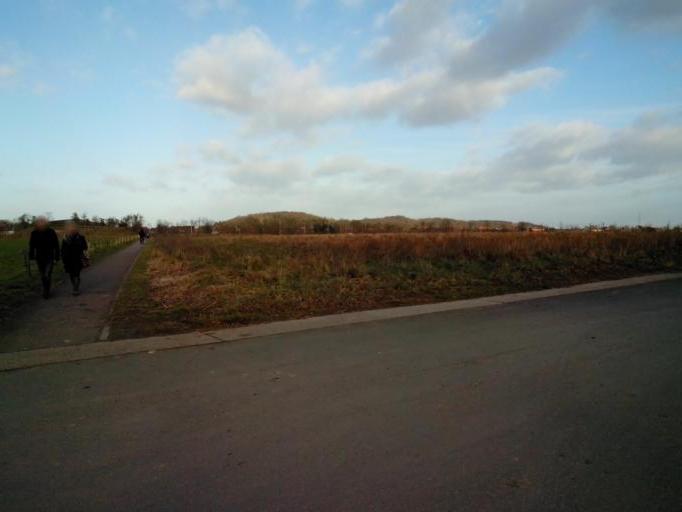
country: BE
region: Flanders
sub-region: Provincie Vlaams-Brabant
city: Leuven
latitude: 50.8659
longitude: 4.7176
